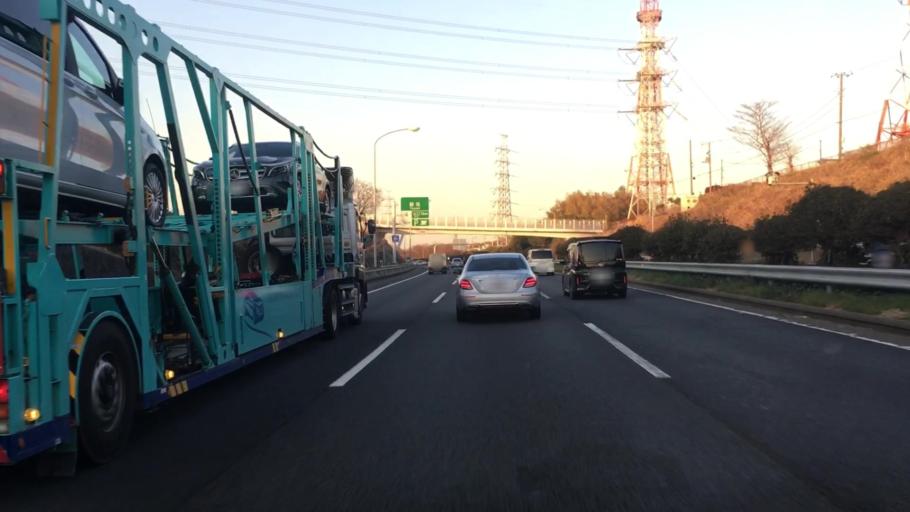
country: JP
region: Kanagawa
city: Yokohama
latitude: 35.5338
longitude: 139.6002
